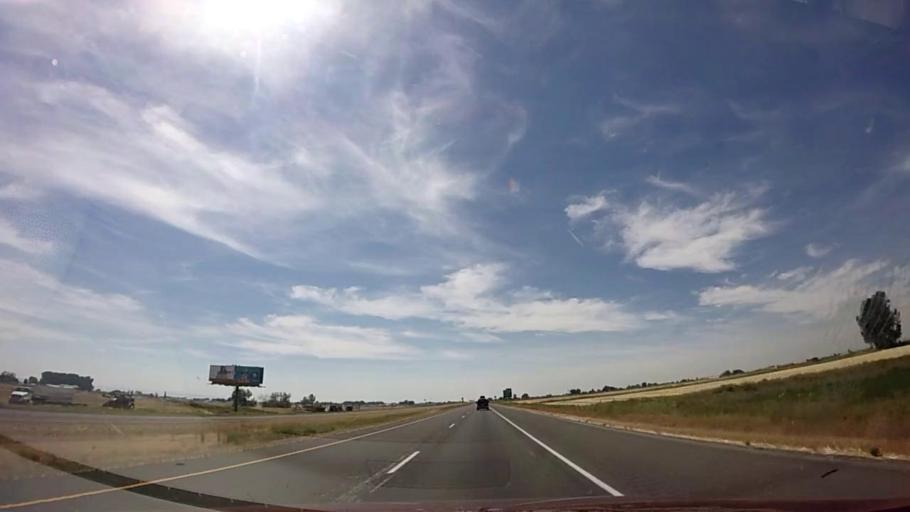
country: US
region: Idaho
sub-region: Minidoka County
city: Heyburn
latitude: 42.5689
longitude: -113.7078
